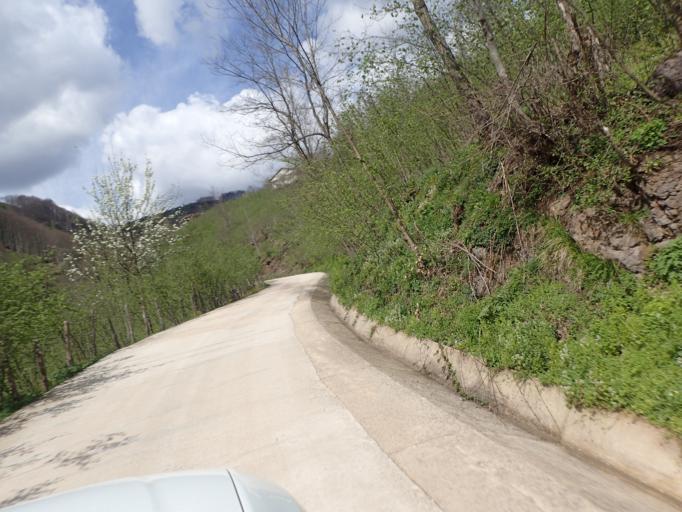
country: TR
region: Ordu
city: Korgan
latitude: 40.7624
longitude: 37.3240
